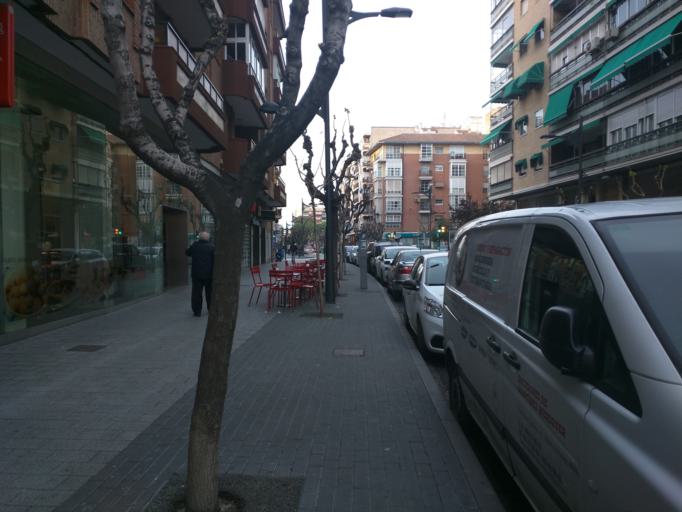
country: ES
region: Murcia
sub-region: Murcia
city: Murcia
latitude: 37.9833
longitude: -1.1221
